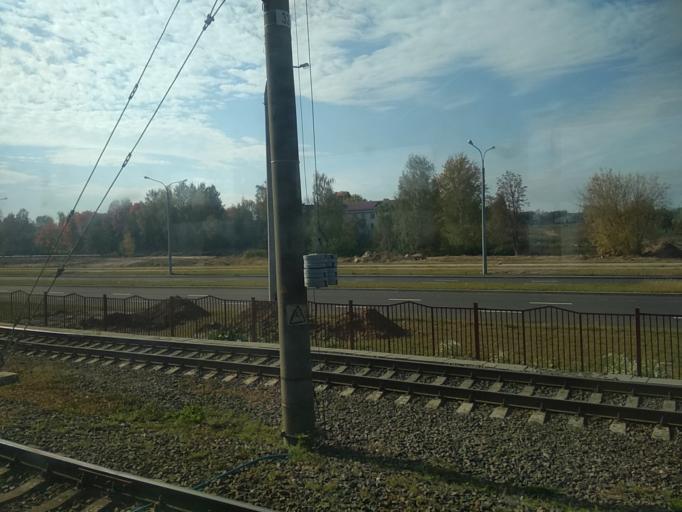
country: BY
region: Minsk
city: Minsk
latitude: 53.8625
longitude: 27.5596
